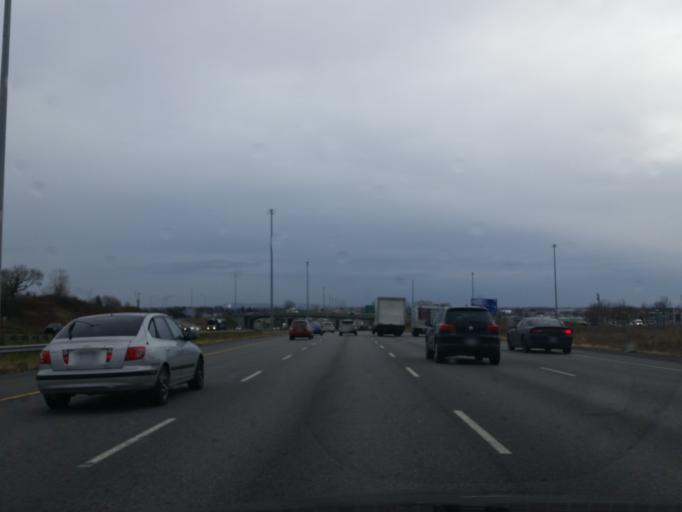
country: CA
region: Quebec
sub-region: Laurentides
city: Blainville
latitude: 45.6473
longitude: -73.8699
